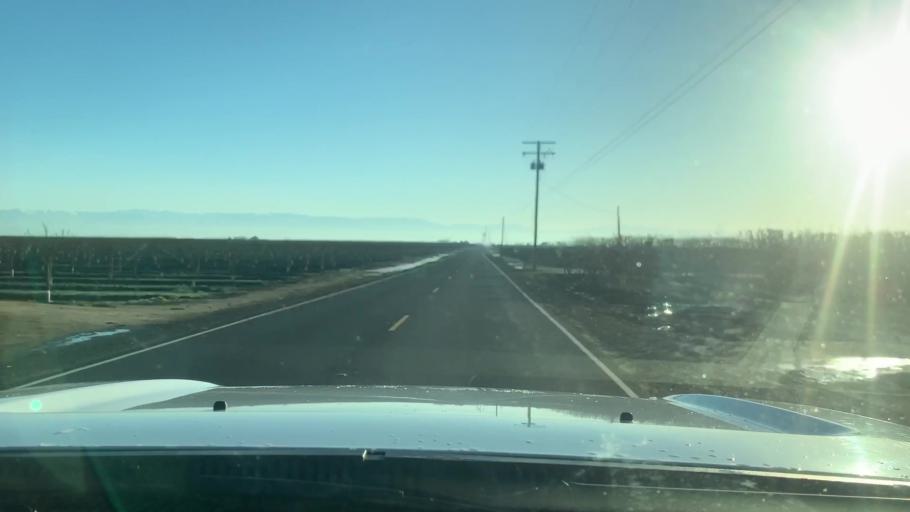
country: US
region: California
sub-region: Tulare County
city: Tulare
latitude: 36.2030
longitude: -119.4647
